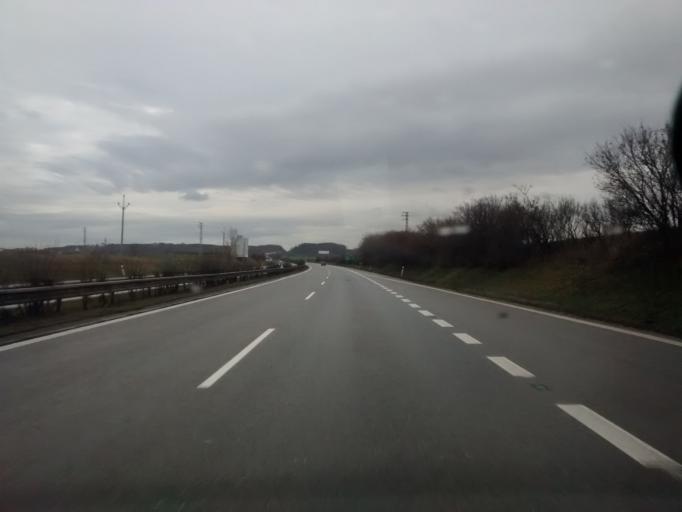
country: CZ
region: Central Bohemia
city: Odolena Voda
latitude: 50.2430
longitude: 14.3790
